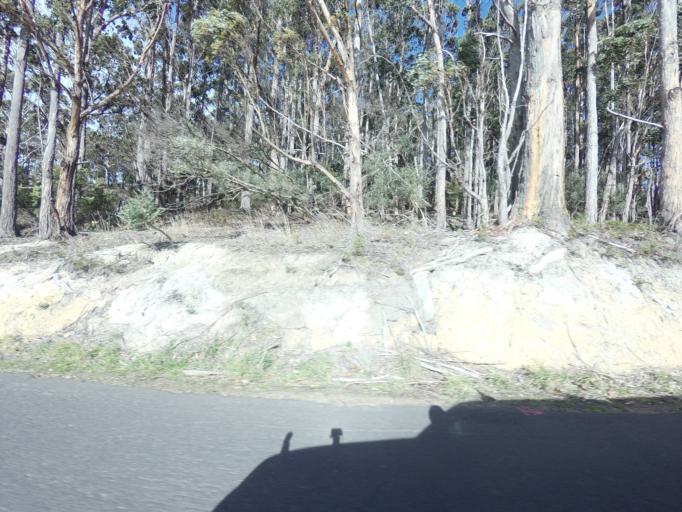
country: AU
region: Tasmania
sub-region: Kingborough
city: Kettering
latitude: -43.1625
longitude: 147.2251
